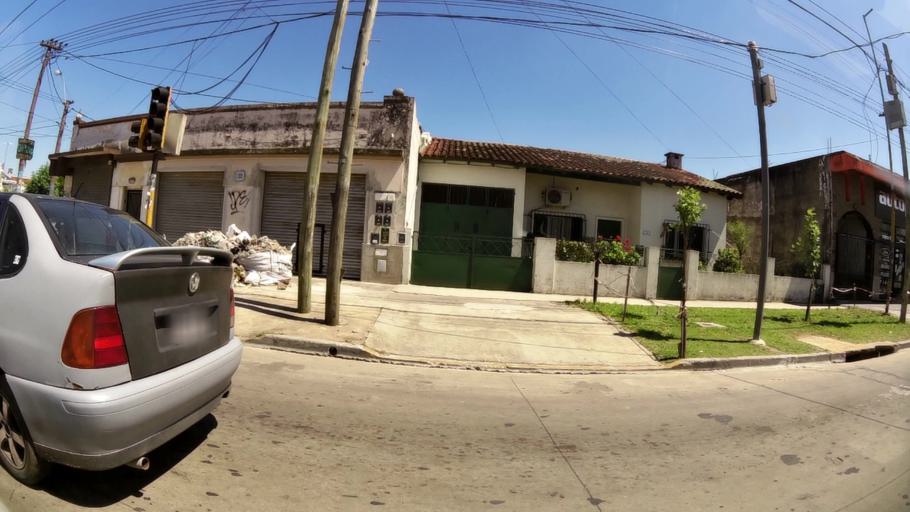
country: AR
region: Buenos Aires
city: Ituzaingo
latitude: -34.6773
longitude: -58.6679
